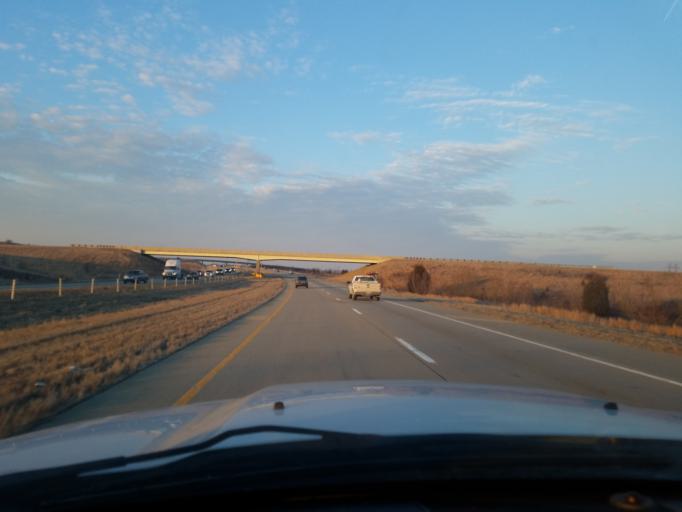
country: US
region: Indiana
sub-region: Vanderburgh County
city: Darmstadt
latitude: 38.1330
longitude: -87.4734
